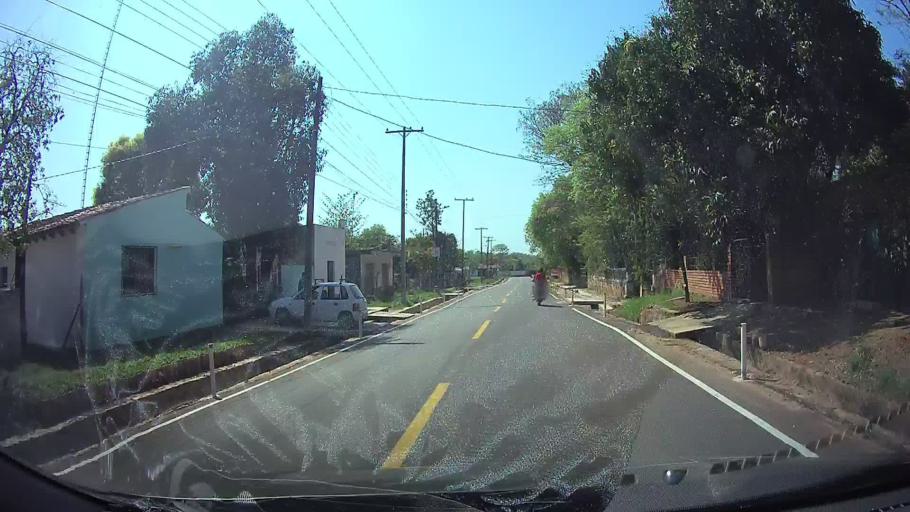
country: PY
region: Central
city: Limpio
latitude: -25.2333
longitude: -57.4905
